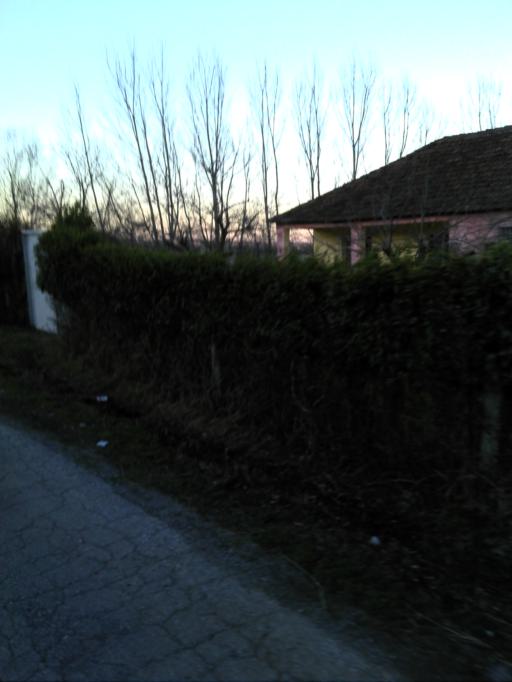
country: AL
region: Shkoder
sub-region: Rrethi i Shkodres
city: Berdica e Madhe
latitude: 42.0132
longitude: 19.4812
